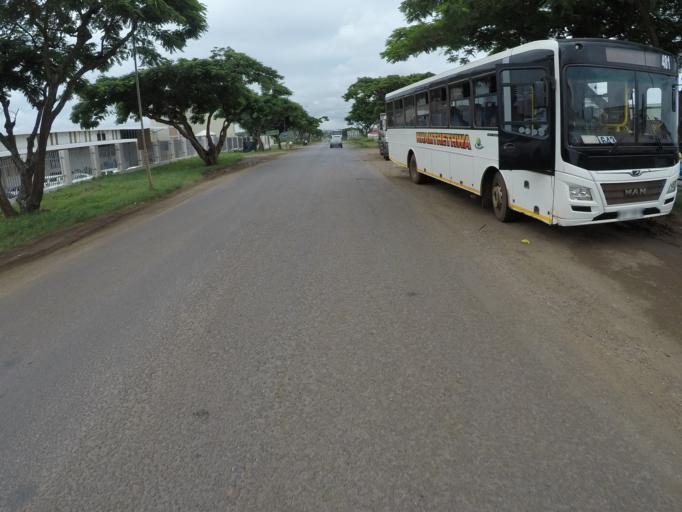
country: ZA
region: KwaZulu-Natal
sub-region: uThungulu District Municipality
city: Empangeni
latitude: -28.7775
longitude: 31.8998
